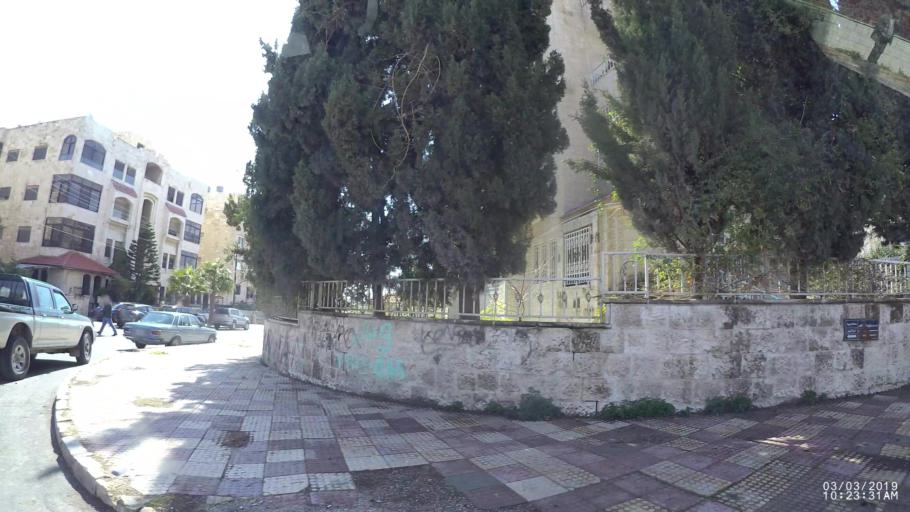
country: JO
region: Amman
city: Al Jubayhah
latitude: 31.9881
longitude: 35.8993
